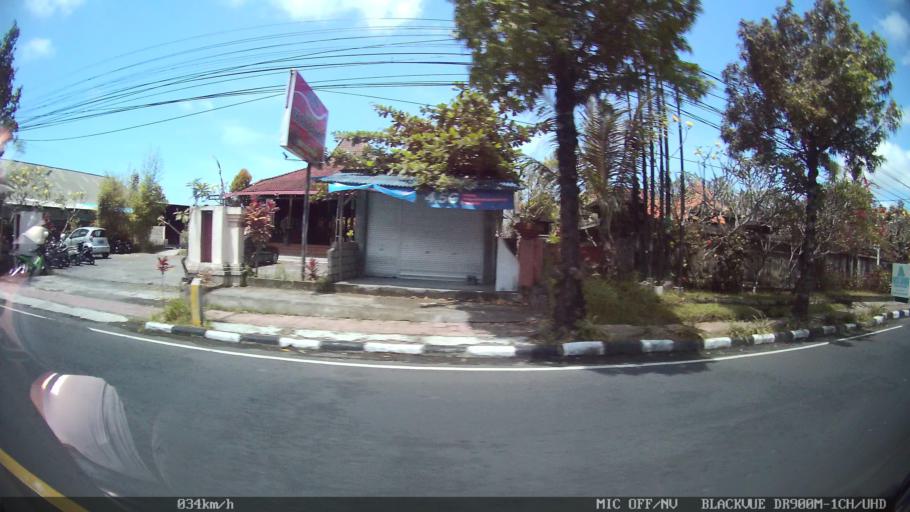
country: ID
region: Bali
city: Banjar Jabejero
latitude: -8.6006
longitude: 115.2670
